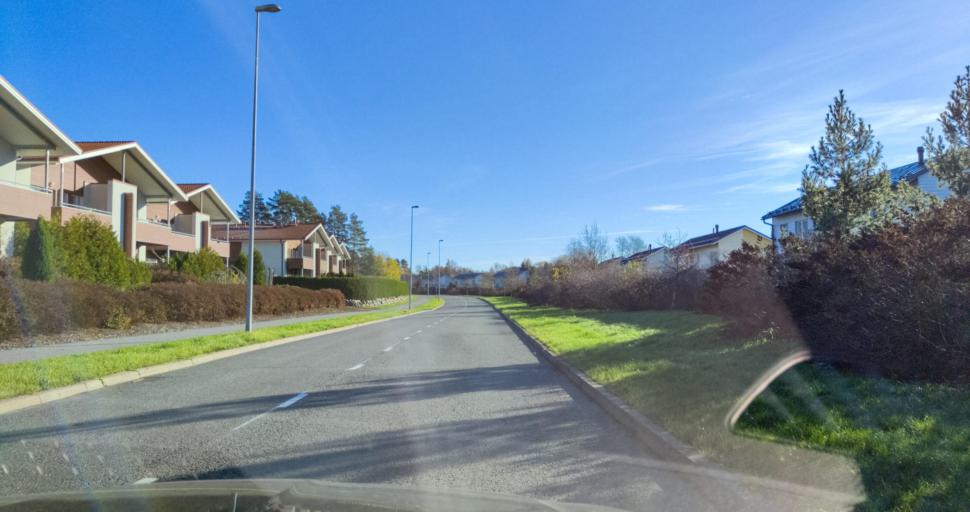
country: FI
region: Varsinais-Suomi
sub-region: Turku
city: Turku
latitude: 60.4099
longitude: 22.2159
